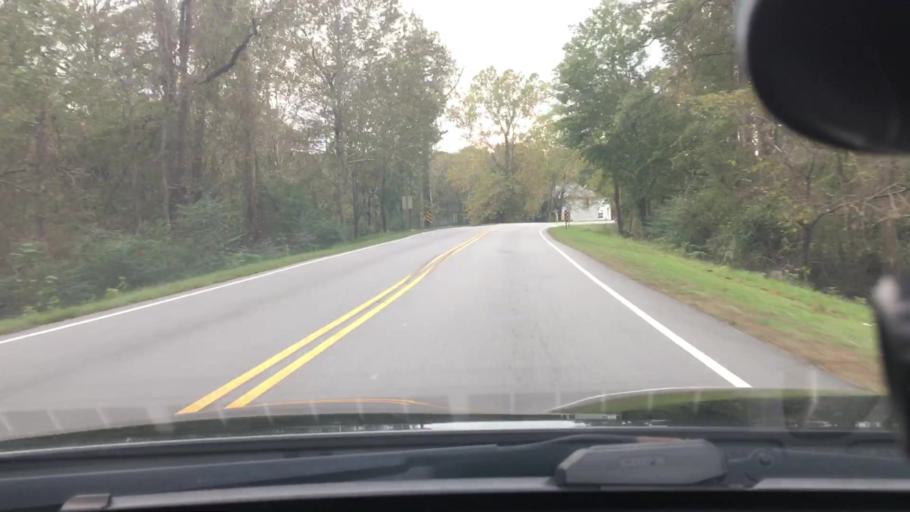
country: US
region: North Carolina
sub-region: Craven County
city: Vanceboro
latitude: 35.2949
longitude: -77.1452
